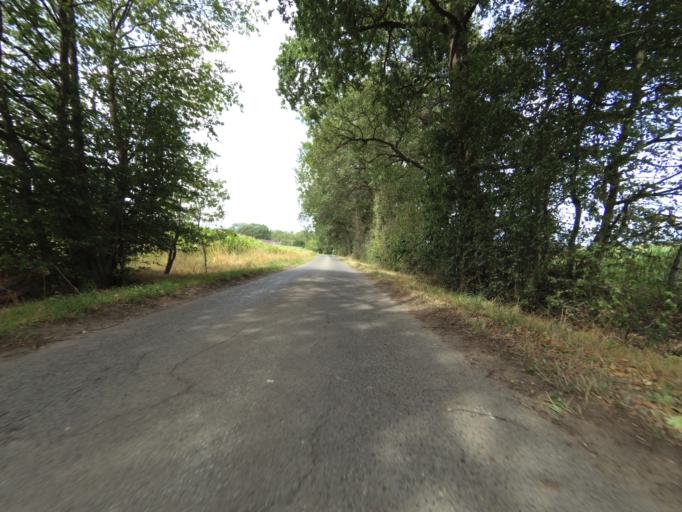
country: DE
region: North Rhine-Westphalia
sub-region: Regierungsbezirk Munster
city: Ahaus
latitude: 52.1426
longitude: 6.9938
